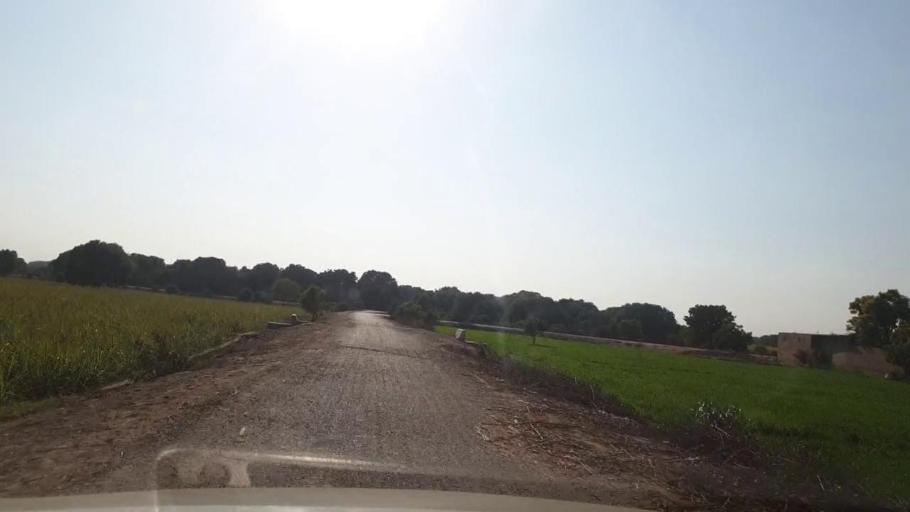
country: PK
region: Sindh
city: Tando Allahyar
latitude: 25.4931
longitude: 68.6465
